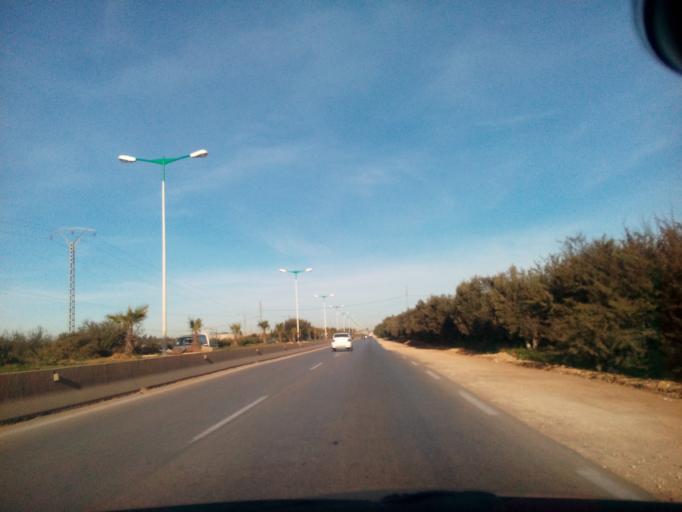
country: DZ
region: Mostaganem
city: Mostaganem
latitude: 35.8601
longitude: 0.1601
